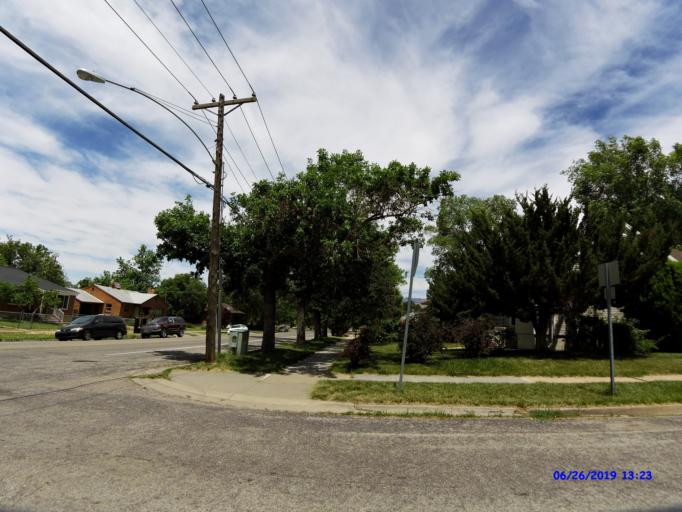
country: US
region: Utah
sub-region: Weber County
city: Ogden
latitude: 41.2090
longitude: -111.9568
